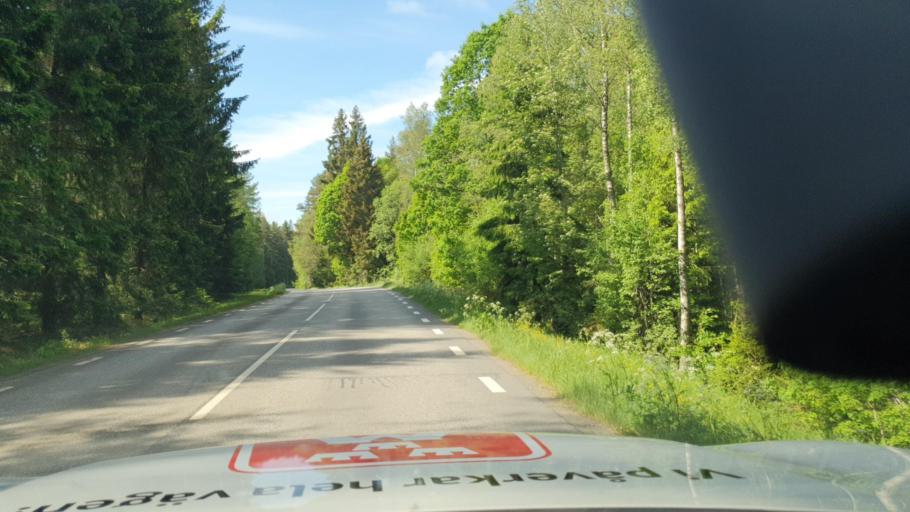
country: SE
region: Vaestra Goetaland
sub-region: Herrljunga Kommun
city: Herrljunga
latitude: 58.0116
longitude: 13.1301
